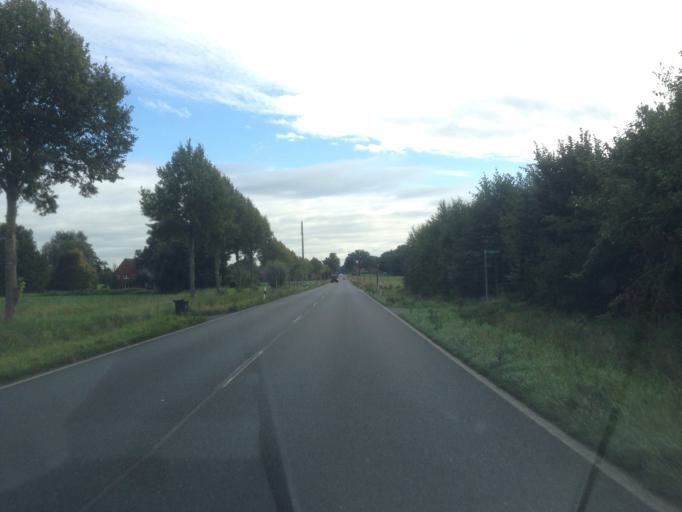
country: DE
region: North Rhine-Westphalia
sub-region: Regierungsbezirk Munster
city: Dulmen
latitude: 51.7927
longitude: 7.3417
